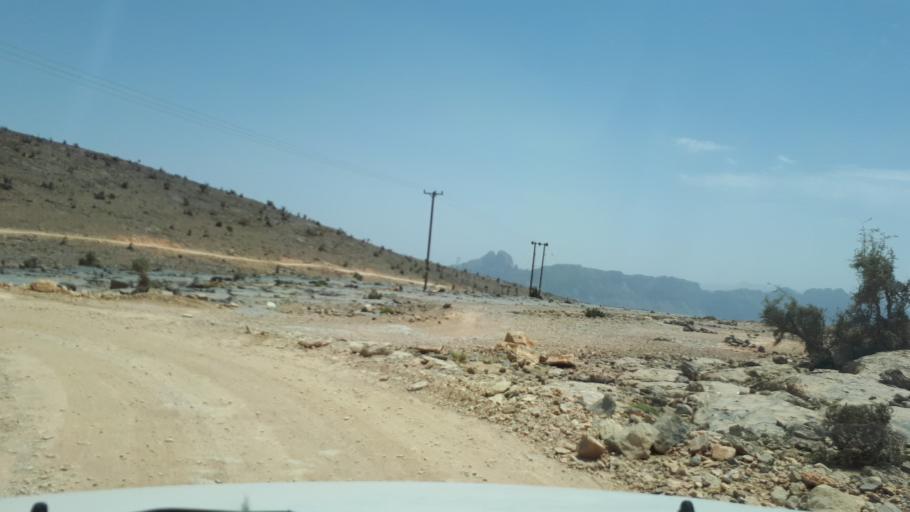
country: OM
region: Muhafazat ad Dakhiliyah
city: Bahla'
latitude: 23.2012
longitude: 57.2004
